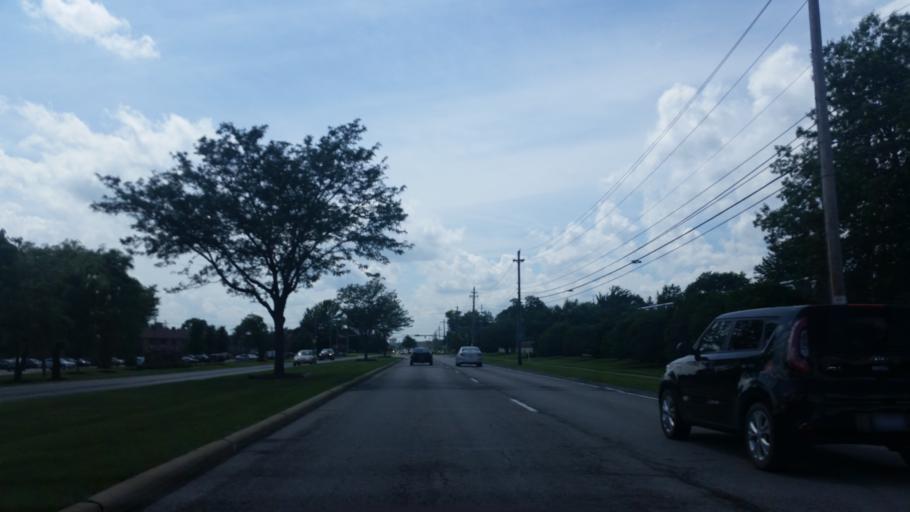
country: US
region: Ohio
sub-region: Cuyahoga County
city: North Olmsted
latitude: 41.4189
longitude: -81.8899
